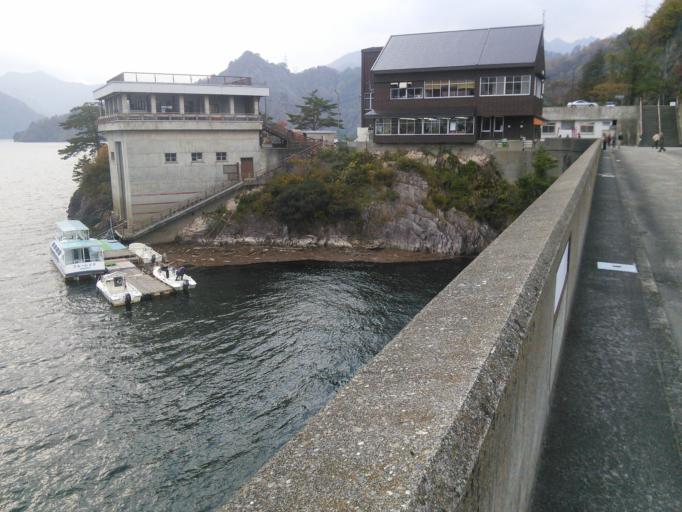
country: JP
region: Niigata
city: Tochio-honcho
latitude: 37.3113
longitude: 139.2855
